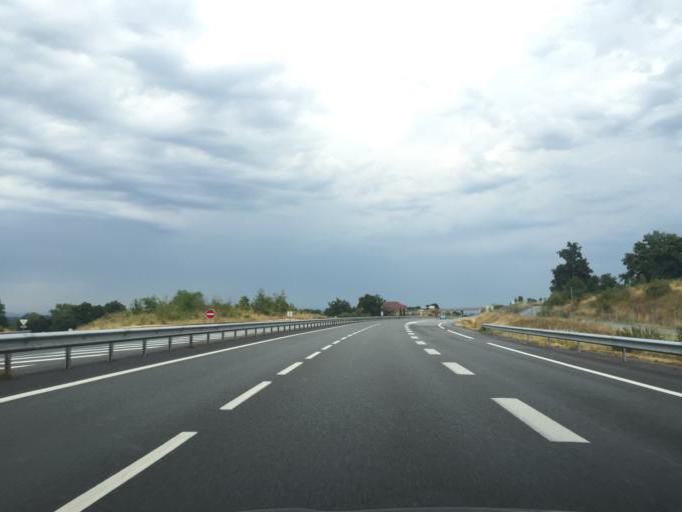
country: FR
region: Rhone-Alpes
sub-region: Departement de la Loire
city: La Pacaudiere
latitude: 46.1919
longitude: 3.8558
